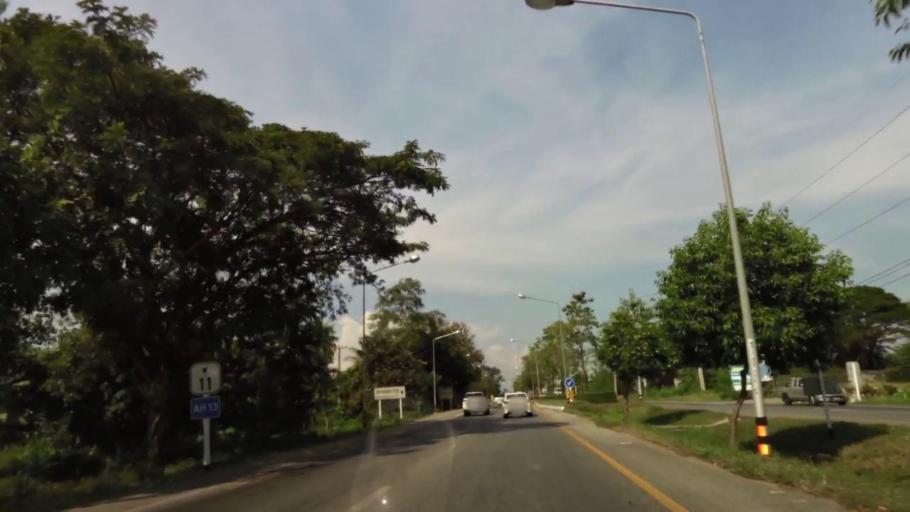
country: TH
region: Uttaradit
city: Uttaradit
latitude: 17.5860
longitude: 100.1379
